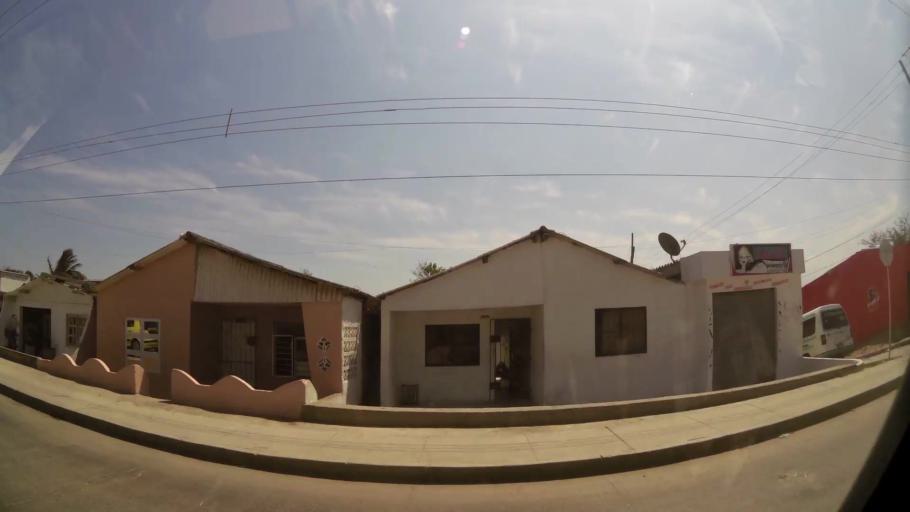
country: CO
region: Atlantico
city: Barranquilla
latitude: 10.9638
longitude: -74.8177
